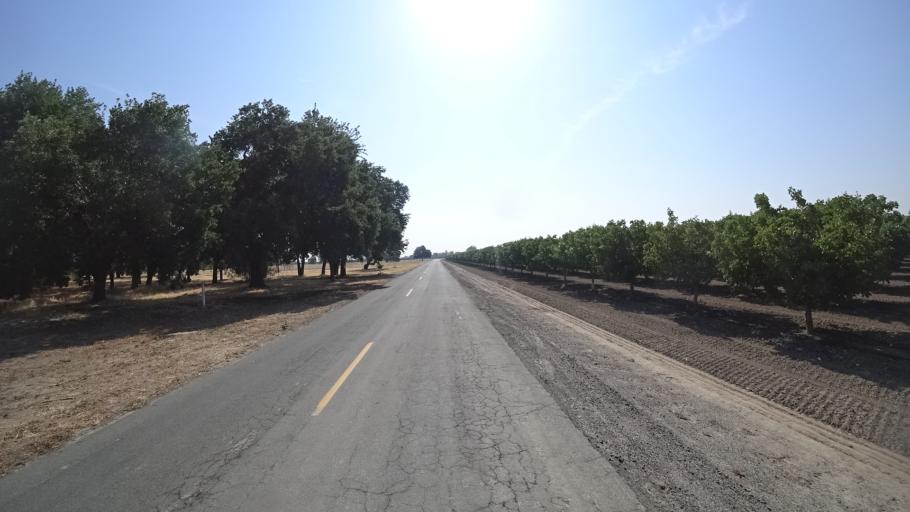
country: US
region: California
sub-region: Kings County
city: Lemoore
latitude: 36.3285
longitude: -119.8559
